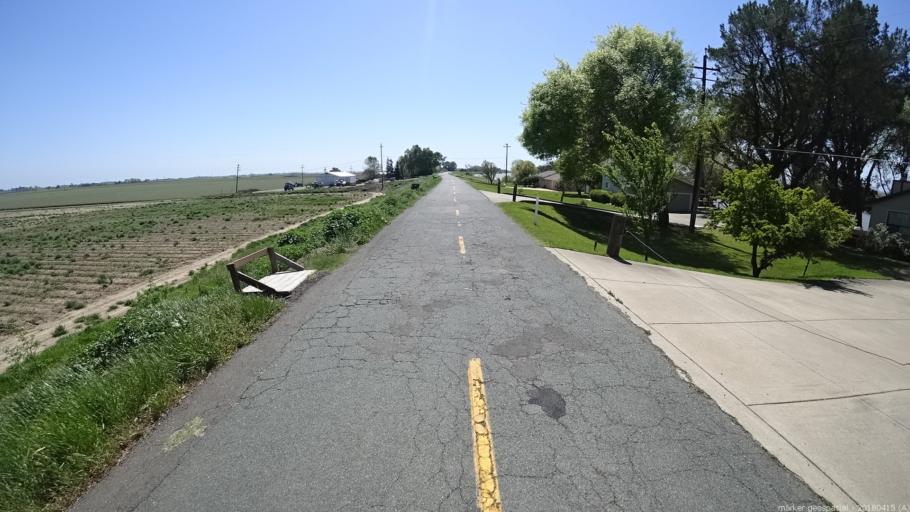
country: US
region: California
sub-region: Sacramento County
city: Walnut Grove
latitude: 38.2493
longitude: -121.6010
